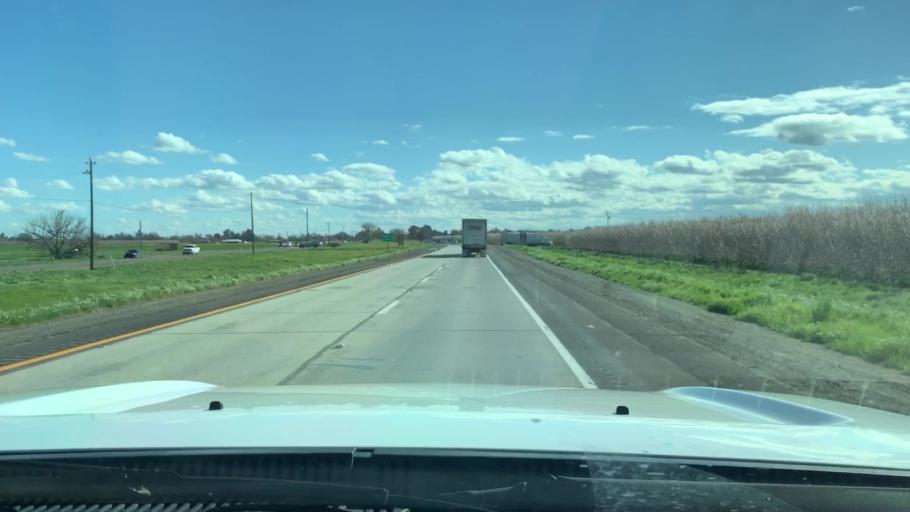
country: US
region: California
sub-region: Fresno County
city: Riverdale
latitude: 36.3824
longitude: -119.8100
